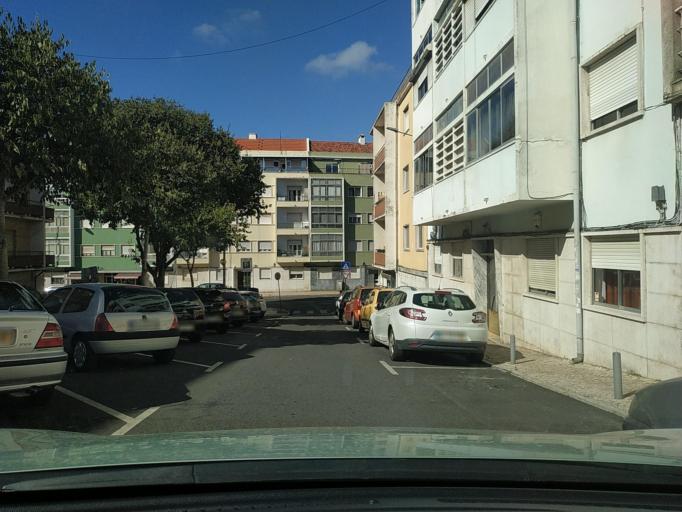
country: PT
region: Lisbon
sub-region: Amadora
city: Amadora
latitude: 38.7589
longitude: -9.2413
